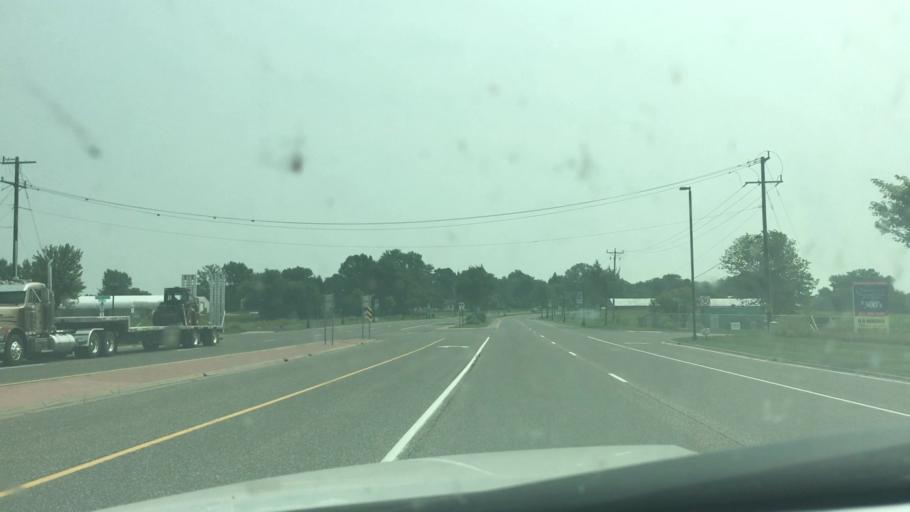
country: US
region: Minnesota
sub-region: Washington County
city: Hugo
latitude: 45.1636
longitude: -93.0089
